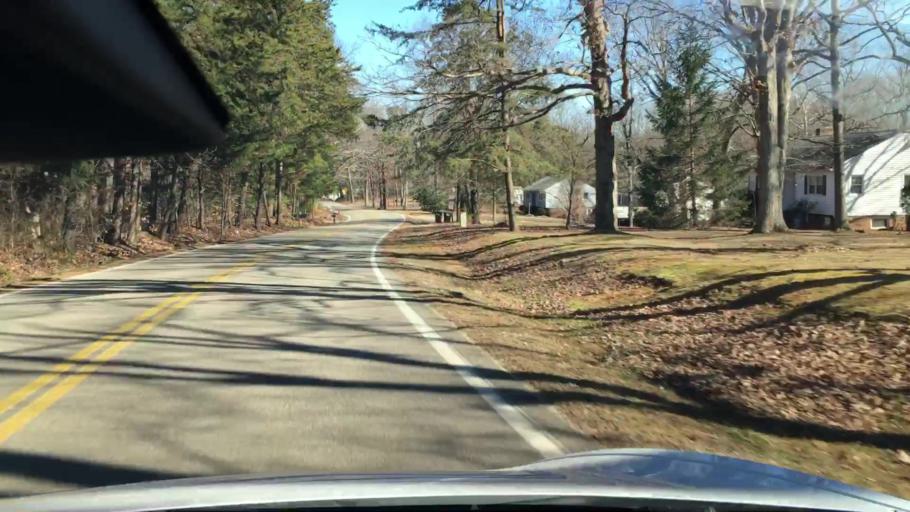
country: US
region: Virginia
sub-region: Powhatan County
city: Powhatan
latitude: 37.5429
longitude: -77.7958
